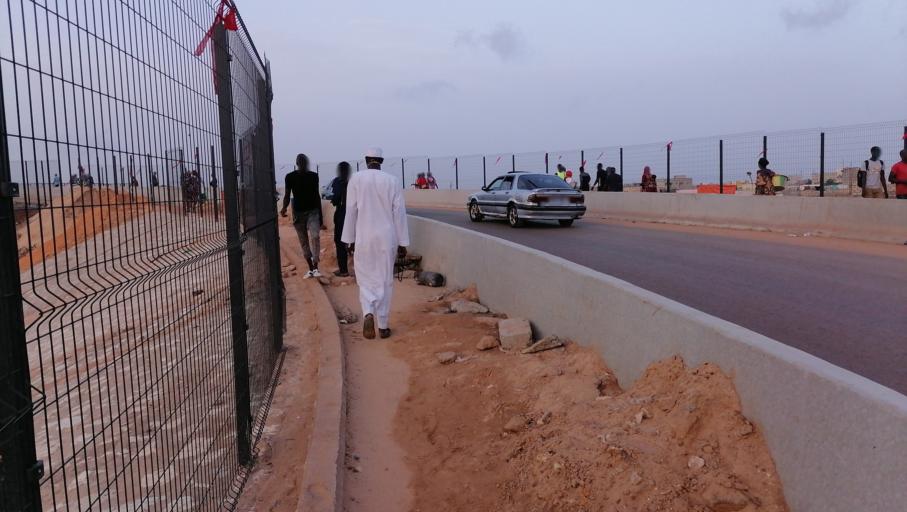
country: SN
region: Dakar
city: Pikine
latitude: 14.7590
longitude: -17.3811
